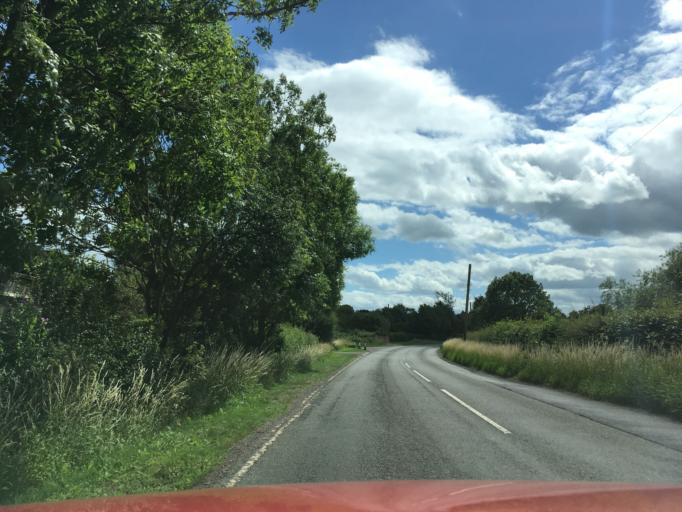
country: GB
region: England
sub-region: Nottinghamshire
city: Cotgrave
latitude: 52.8962
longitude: -1.0801
